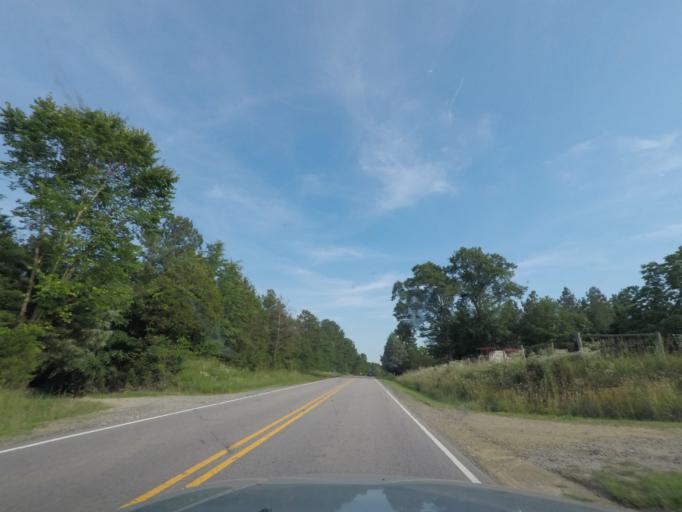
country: US
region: Virginia
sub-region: Mecklenburg County
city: Clarksville
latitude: 36.5357
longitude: -78.5376
